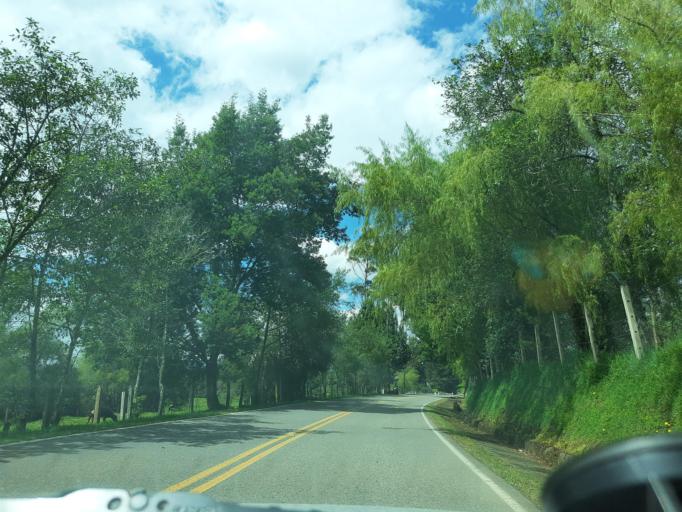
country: CO
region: Boyaca
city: Chiquinquira
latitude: 5.5996
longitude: -73.7178
